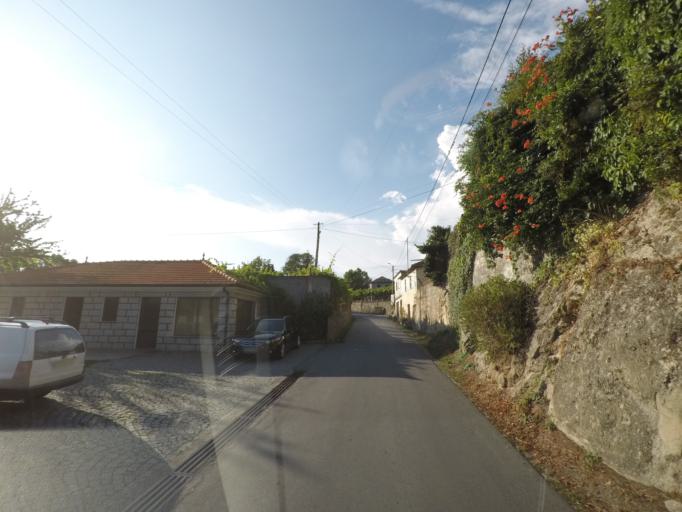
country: PT
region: Vila Real
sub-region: Mesao Frio
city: Mesao Frio
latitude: 41.1670
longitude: -7.9272
